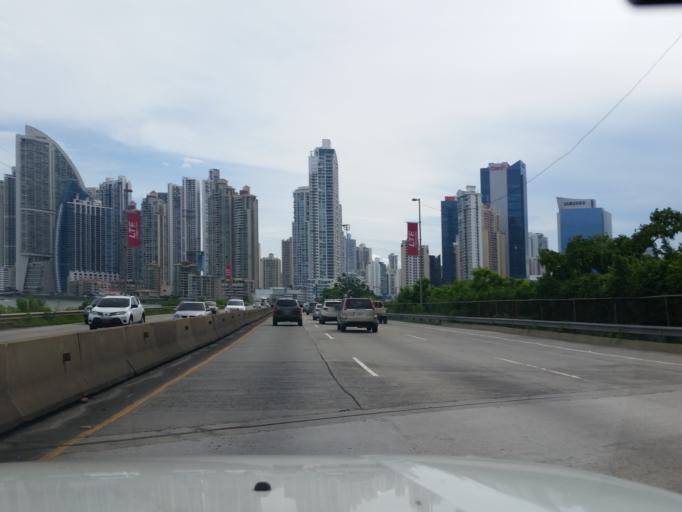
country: PA
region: Panama
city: Panama
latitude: 8.9857
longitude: -79.5016
